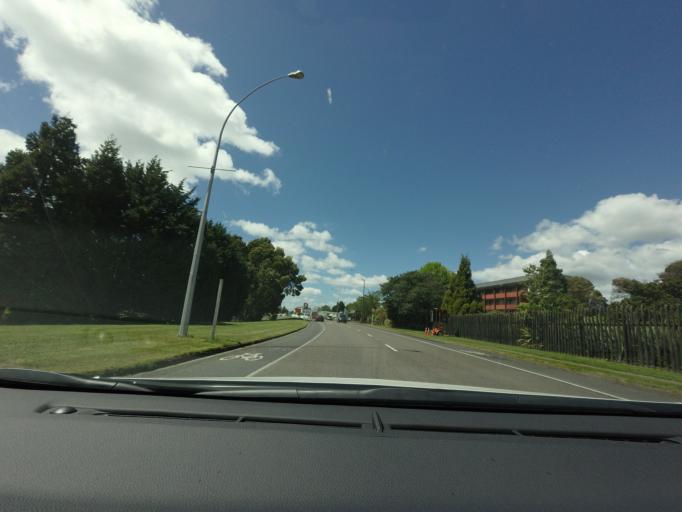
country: NZ
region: Bay of Plenty
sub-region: Rotorua District
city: Rotorua
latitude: -38.1624
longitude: 176.2520
